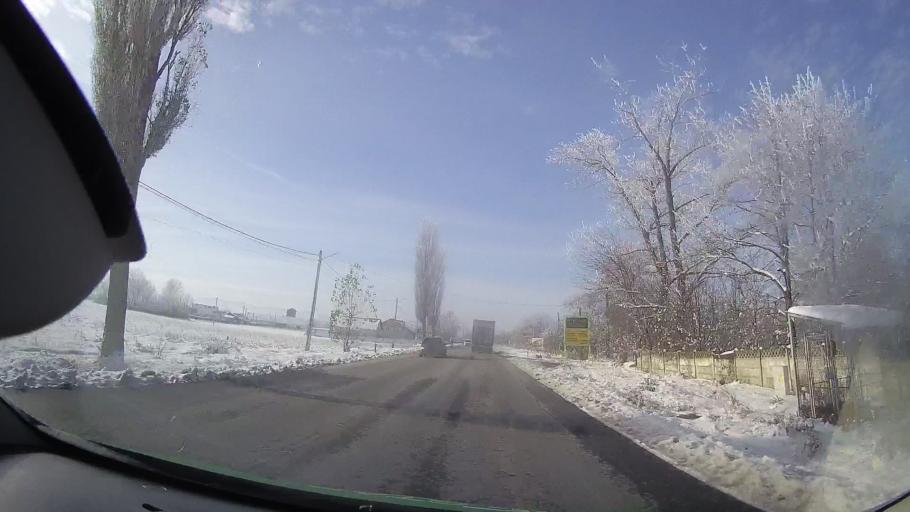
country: RO
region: Neamt
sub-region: Oras Targu Neamt
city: Targu Neamt
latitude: 47.2091
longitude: 26.4034
